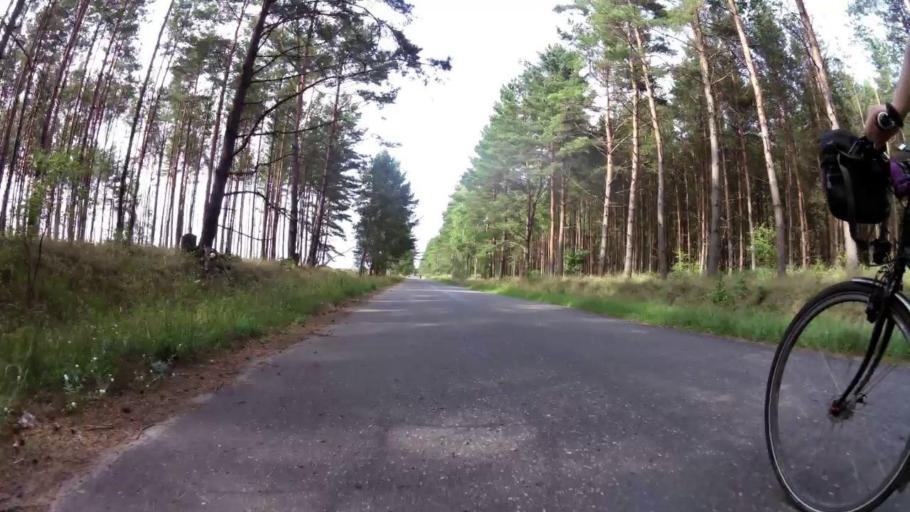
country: PL
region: West Pomeranian Voivodeship
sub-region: Powiat stargardzki
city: Insko
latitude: 53.3889
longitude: 15.5957
